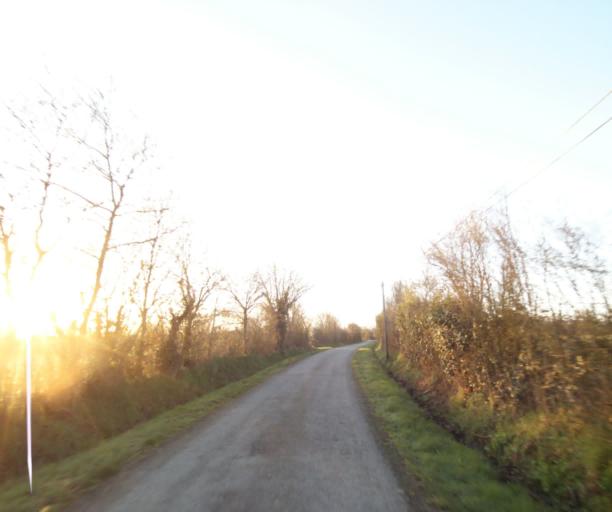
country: FR
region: Pays de la Loire
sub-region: Departement de la Loire-Atlantique
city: Bouvron
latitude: 47.4215
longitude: -1.8805
